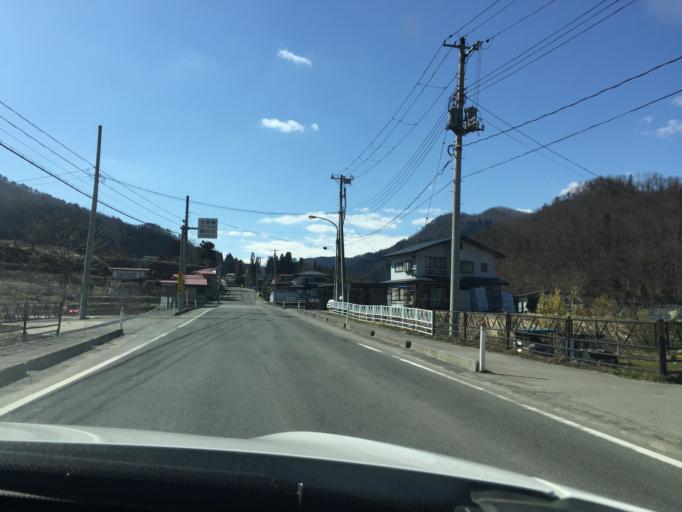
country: JP
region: Yamagata
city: Sagae
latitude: 38.2911
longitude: 140.1175
